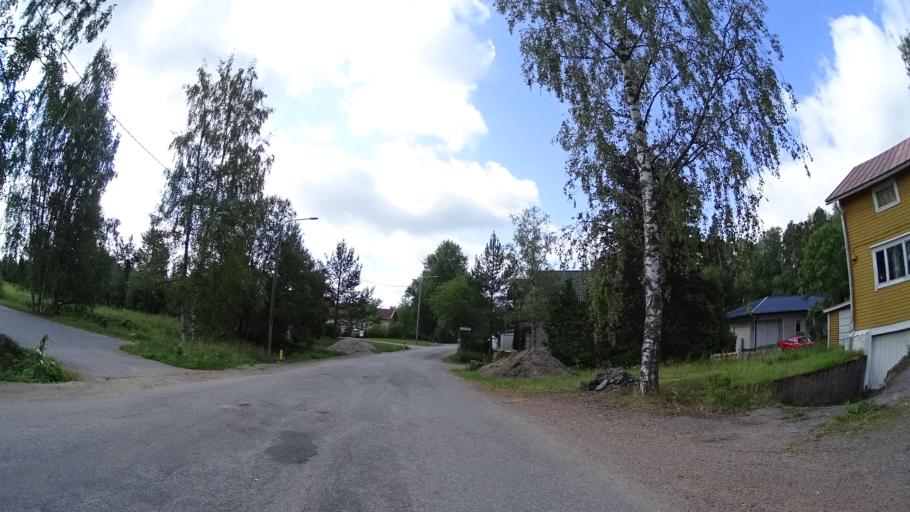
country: FI
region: Uusimaa
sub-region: Helsinki
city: Helsinki
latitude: 60.2791
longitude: 24.9168
